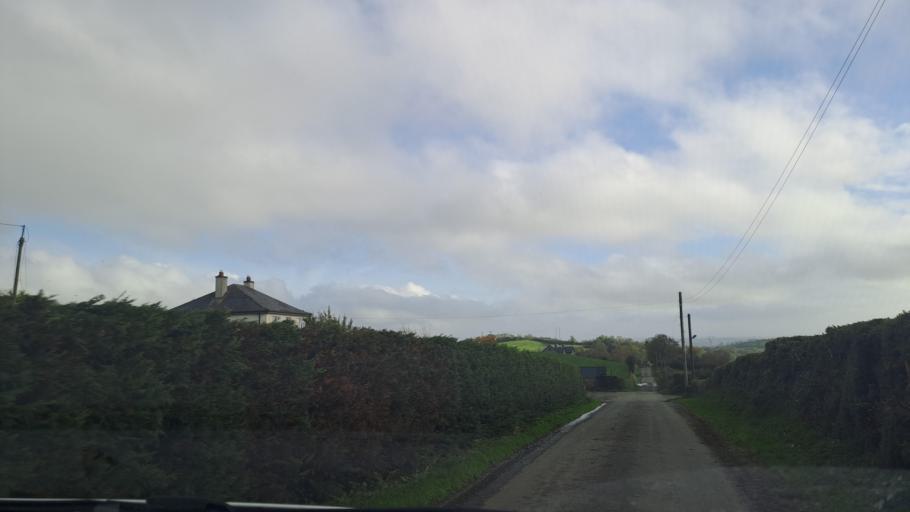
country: IE
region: Ulster
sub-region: County Monaghan
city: Carrickmacross
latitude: 54.0241
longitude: -6.7697
